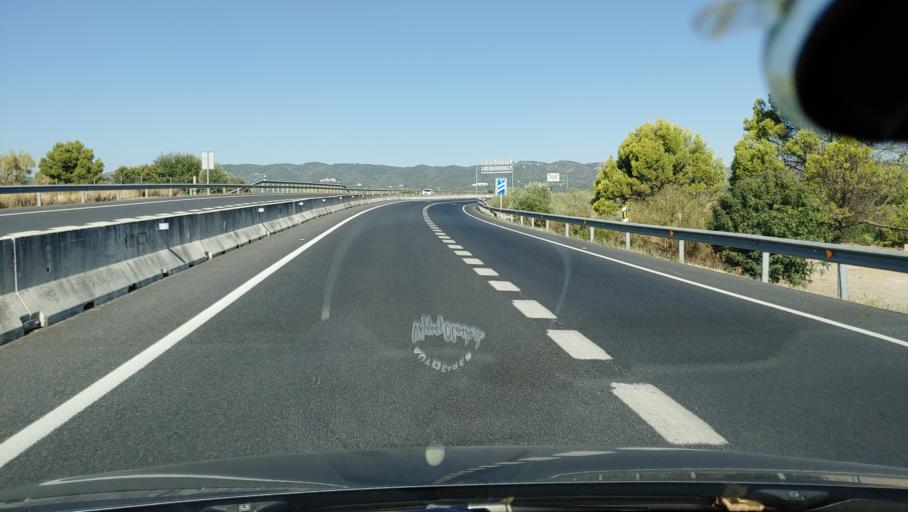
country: ES
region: Andalusia
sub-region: Province of Cordoba
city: Cordoba
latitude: 37.9142
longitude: -4.7562
